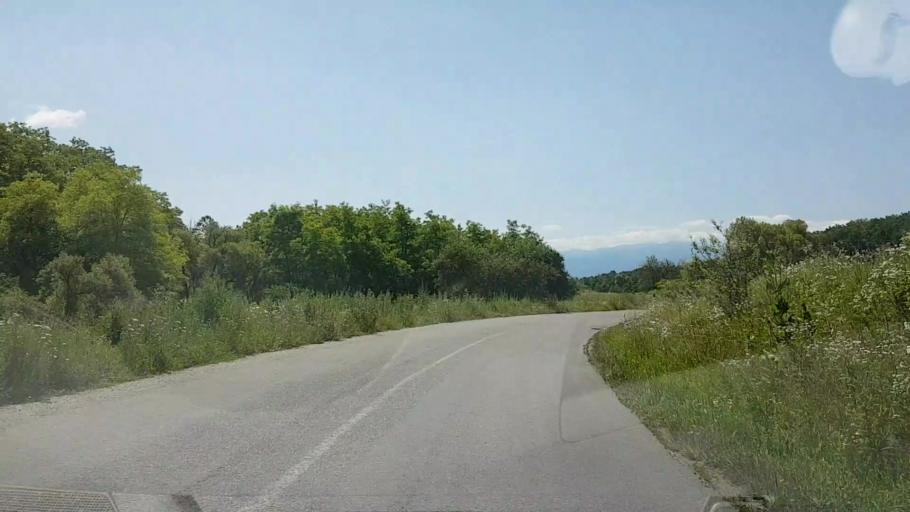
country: RO
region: Brasov
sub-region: Comuna Cincu
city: Cincu
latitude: 45.8850
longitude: 24.8141
